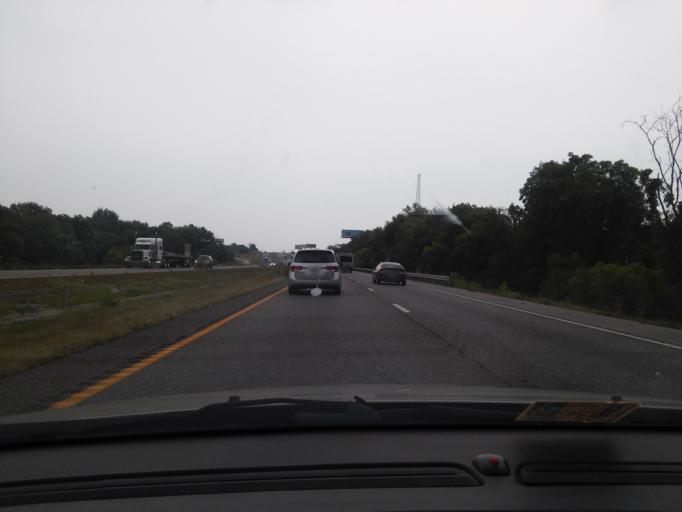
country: US
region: Missouri
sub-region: Boone County
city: Hallsville
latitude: 38.9544
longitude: -92.1529
